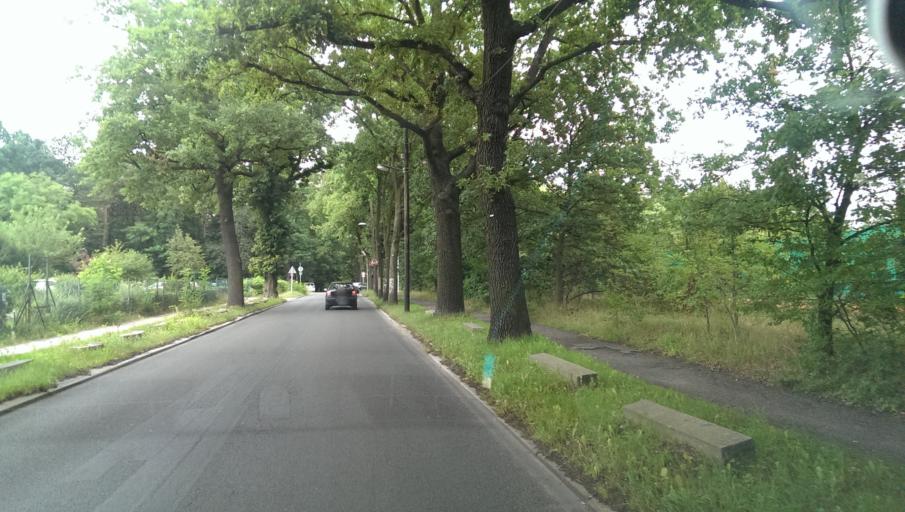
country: DE
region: Brandenburg
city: Kleinmachnow
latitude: 52.4227
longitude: 13.2250
